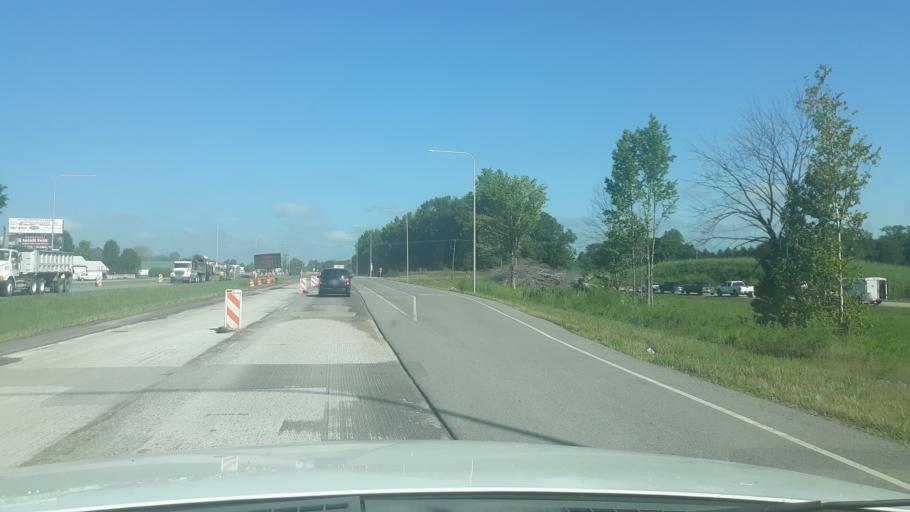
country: US
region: Illinois
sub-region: Williamson County
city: Marion
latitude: 37.7334
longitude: -88.8910
